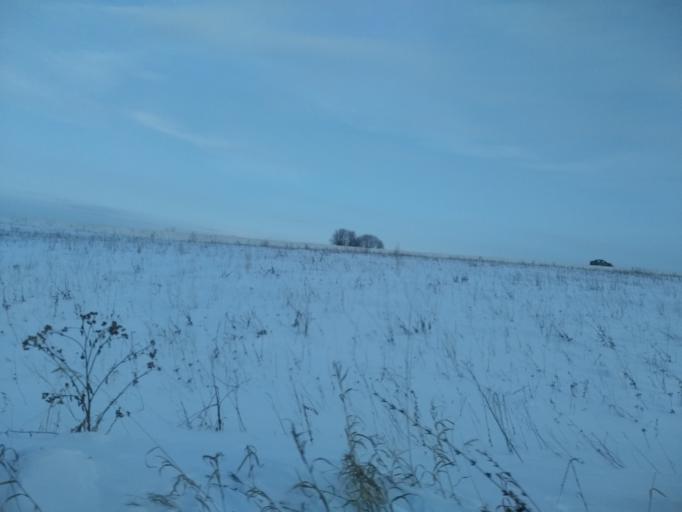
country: RU
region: Bashkortostan
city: Iglino
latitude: 54.7696
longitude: 56.5499
